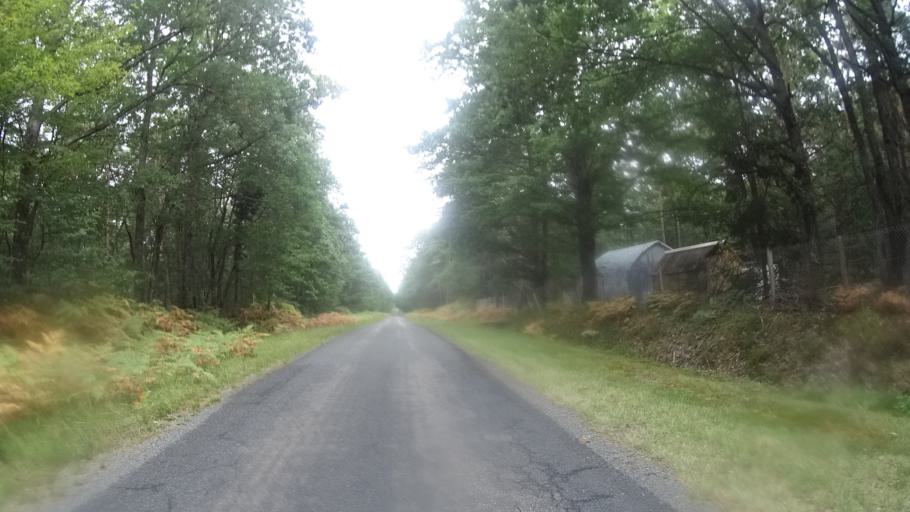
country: FR
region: Centre
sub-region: Departement du Loiret
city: Vitry-aux-Loges
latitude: 48.0258
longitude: 2.2589
